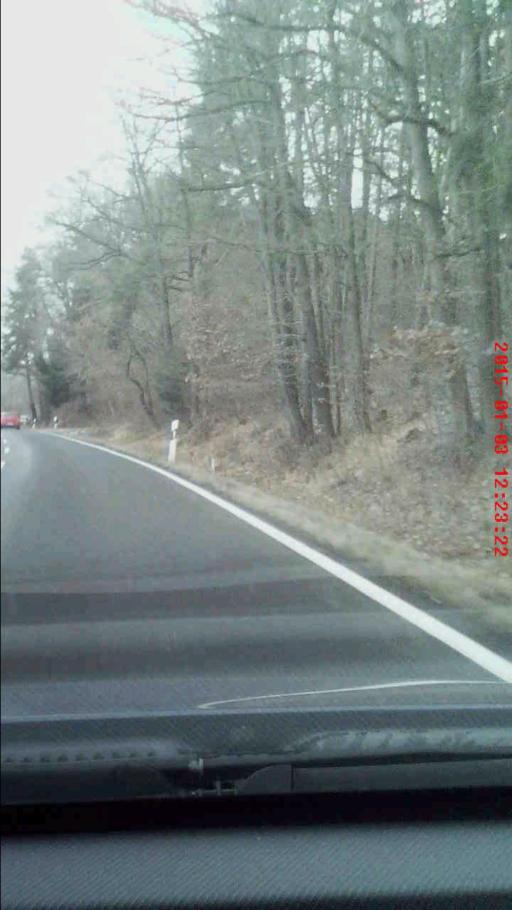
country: DE
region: Thuringia
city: Kranichfeld
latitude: 50.8594
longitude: 11.2249
